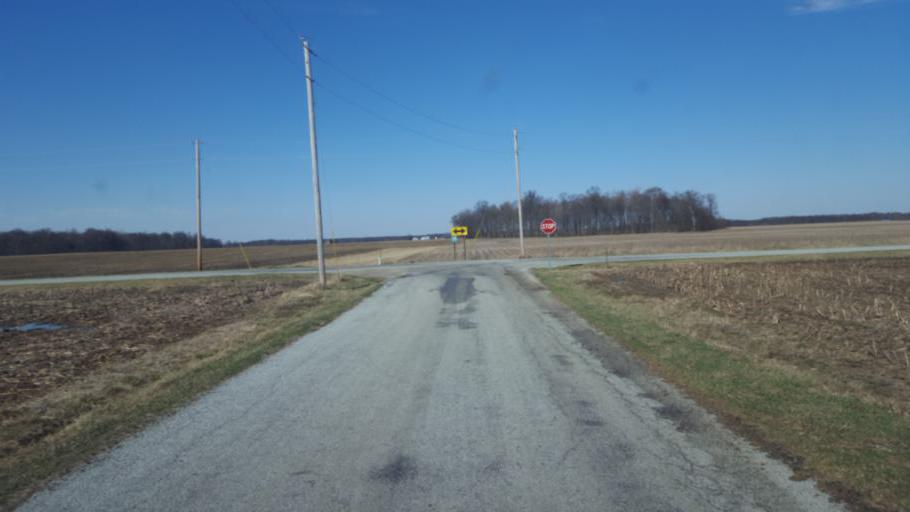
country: US
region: Ohio
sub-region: Hardin County
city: Forest
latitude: 40.6872
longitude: -83.4401
